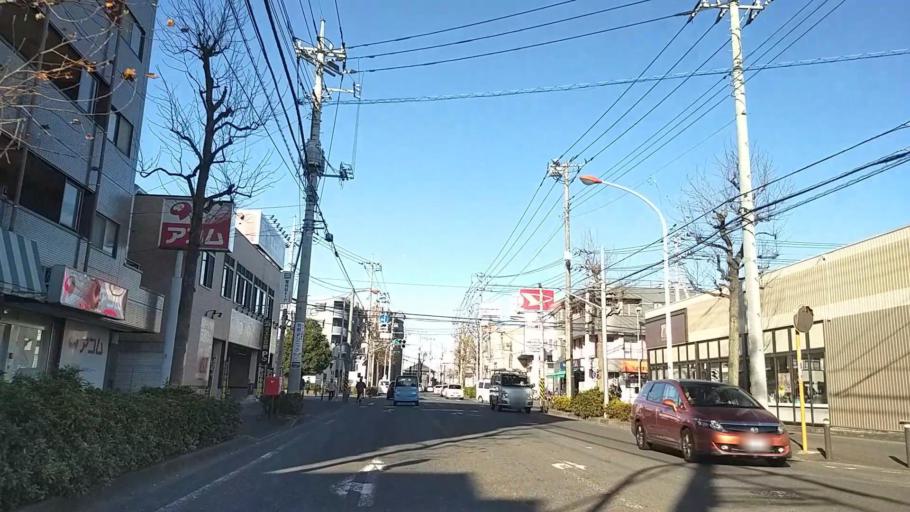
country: JP
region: Tokyo
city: Chofugaoka
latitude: 35.6236
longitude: 139.5459
